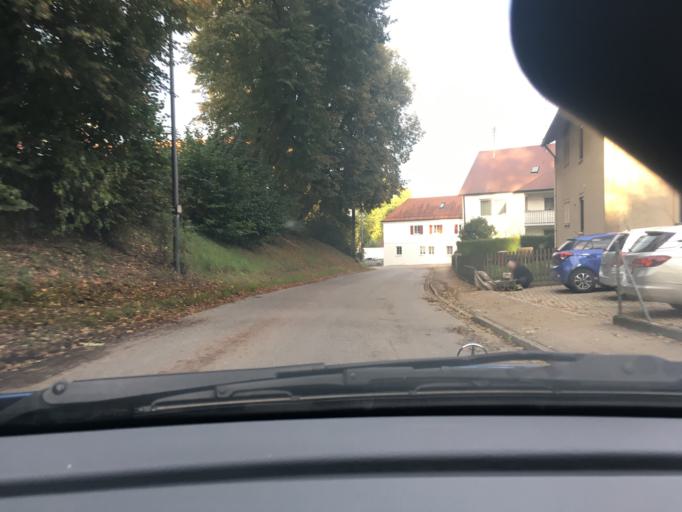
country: DE
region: Bavaria
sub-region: Swabia
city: Gablingen
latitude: 48.4284
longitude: 10.8163
